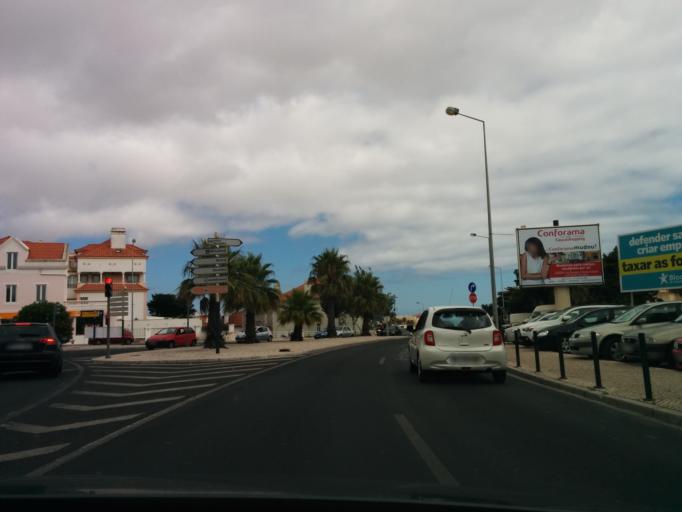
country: PT
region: Lisbon
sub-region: Cascais
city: Estoril
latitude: 38.7033
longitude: -9.3950
